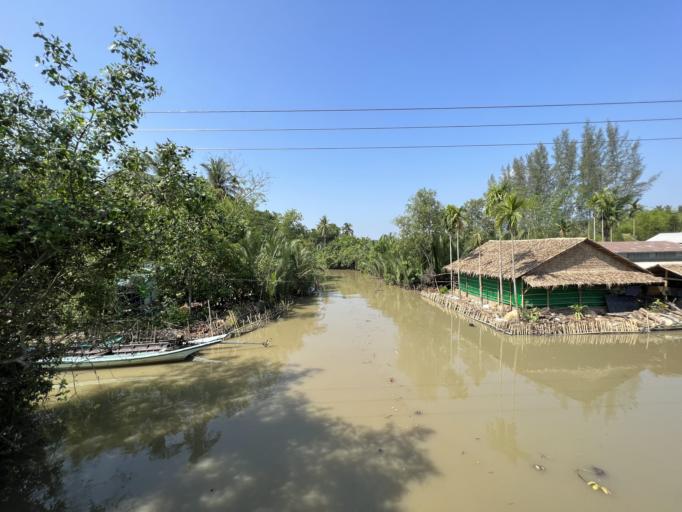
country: MM
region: Ayeyarwady
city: Kyaiklat
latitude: 16.4277
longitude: 95.7925
